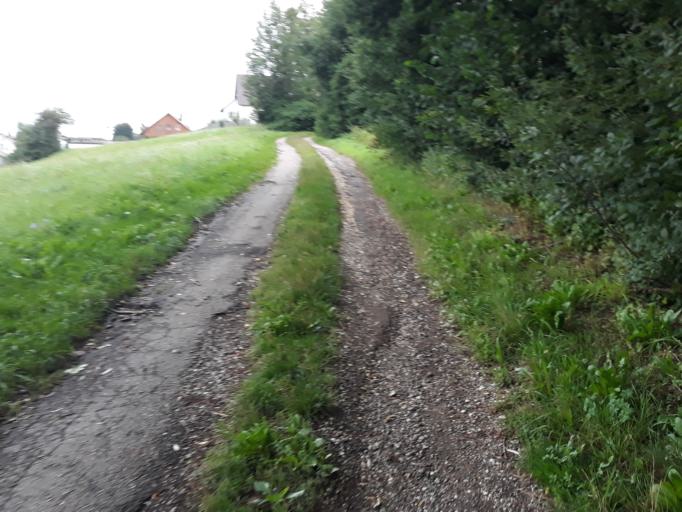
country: DE
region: Bavaria
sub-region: Swabia
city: Wasserburg
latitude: 48.4395
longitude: 10.2672
